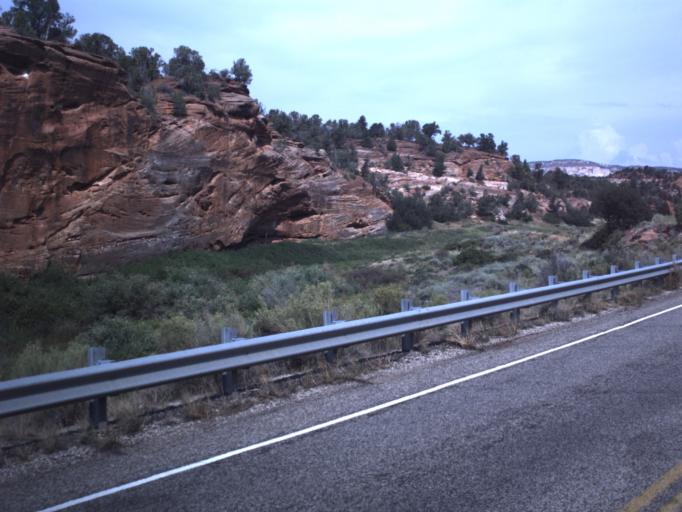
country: US
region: Utah
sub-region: Kane County
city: Kanab
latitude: 37.1374
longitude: -112.5659
